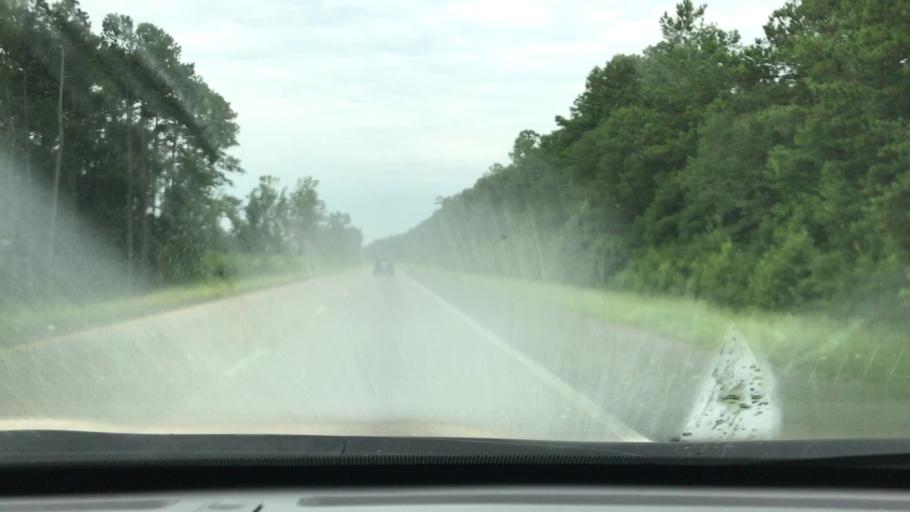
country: US
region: South Carolina
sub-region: Colleton County
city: Walterboro
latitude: 32.8644
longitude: -80.7257
